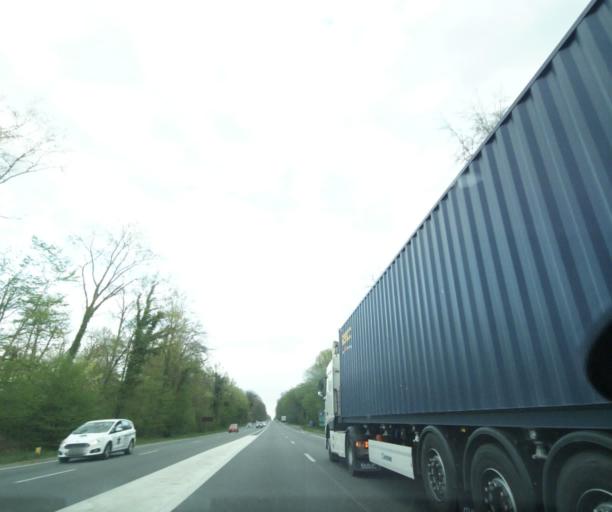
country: FR
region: Ile-de-France
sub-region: Departement de Seine-et-Marne
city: Fontainebleau
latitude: 48.4289
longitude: 2.6627
